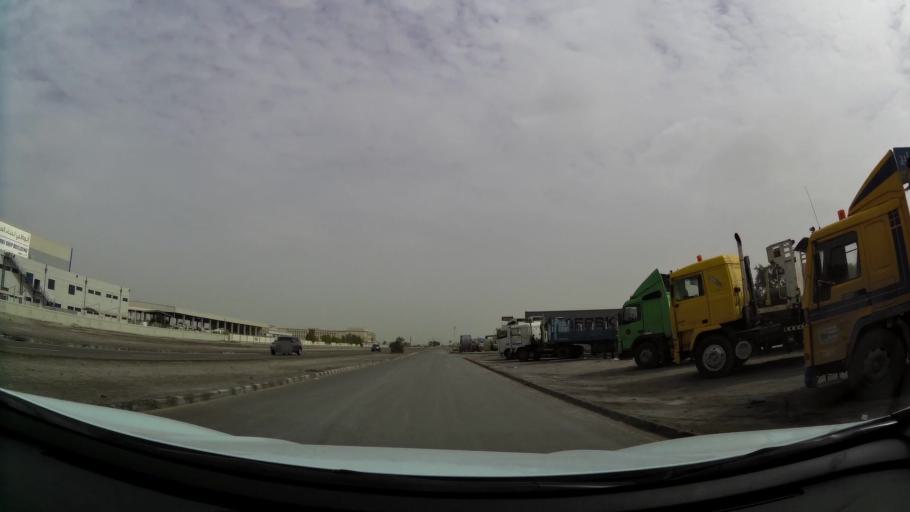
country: AE
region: Abu Dhabi
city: Abu Dhabi
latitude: 24.3534
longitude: 54.4668
